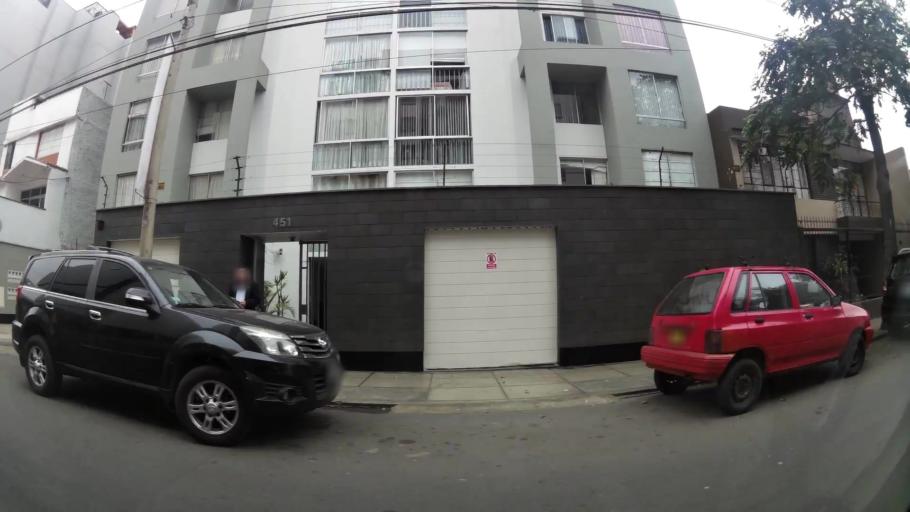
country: PE
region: Lima
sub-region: Lima
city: San Isidro
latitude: -12.1169
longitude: -77.0332
